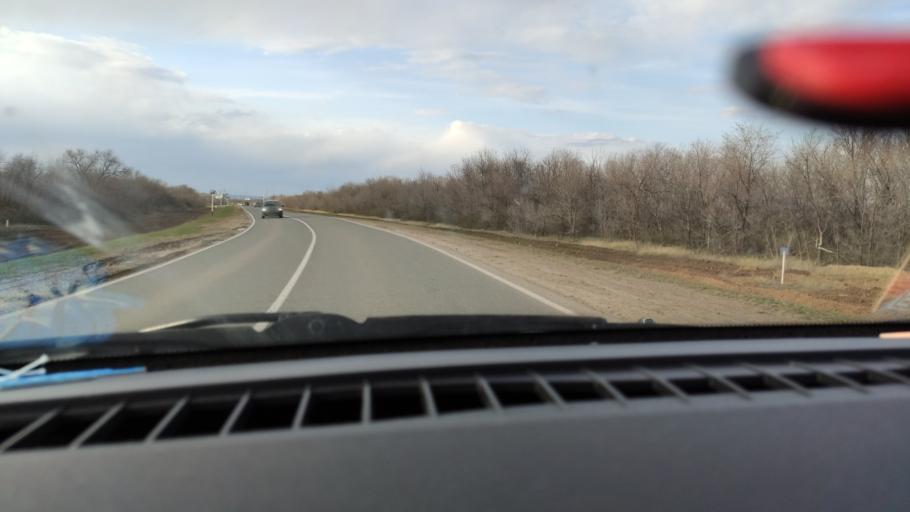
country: RU
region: Saratov
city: Privolzhskiy
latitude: 51.3749
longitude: 46.0450
